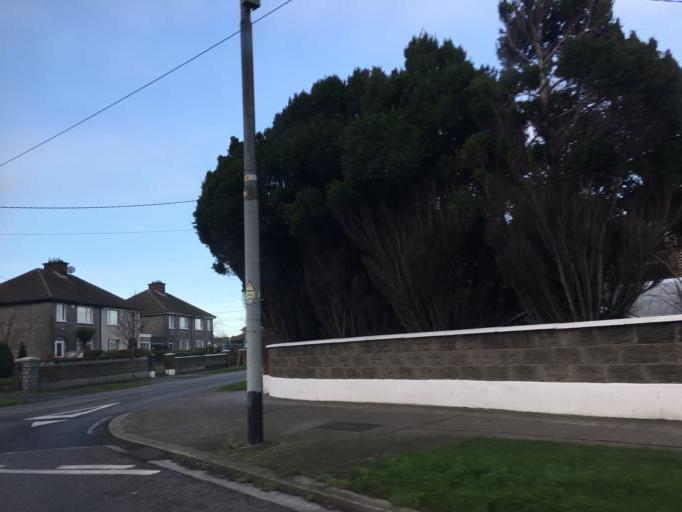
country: IE
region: Leinster
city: Ballymun
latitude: 53.3907
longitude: -6.2793
